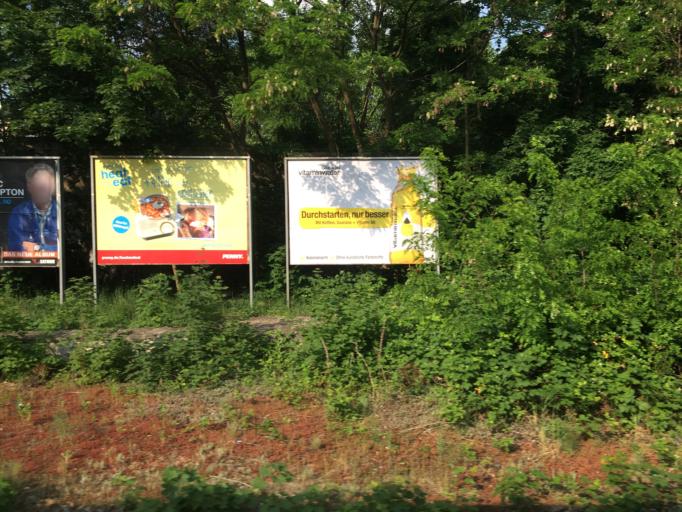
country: DE
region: Berlin
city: Halensee
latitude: 52.4961
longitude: 13.2904
